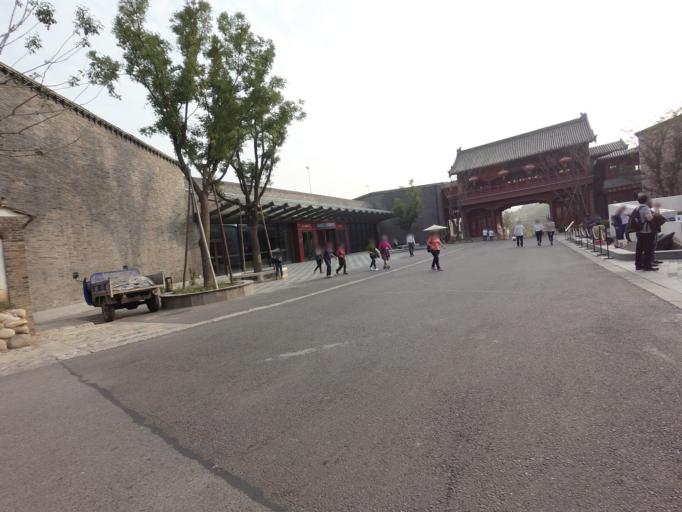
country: CN
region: Beijing
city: Xinchengzi
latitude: 40.6520
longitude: 117.2690
